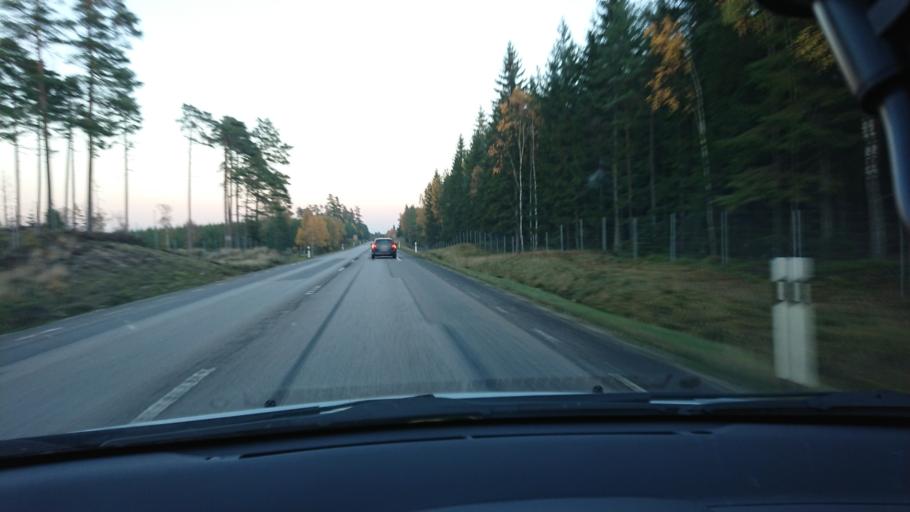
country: SE
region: Halland
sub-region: Laholms Kommun
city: Knared
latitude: 56.7264
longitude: 13.3877
